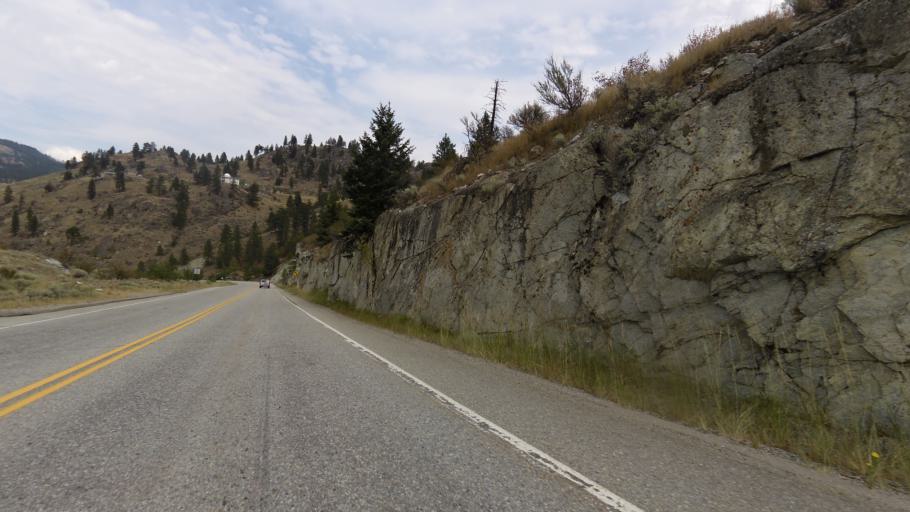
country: CA
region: British Columbia
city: Osoyoos
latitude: 49.0120
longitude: -119.4038
